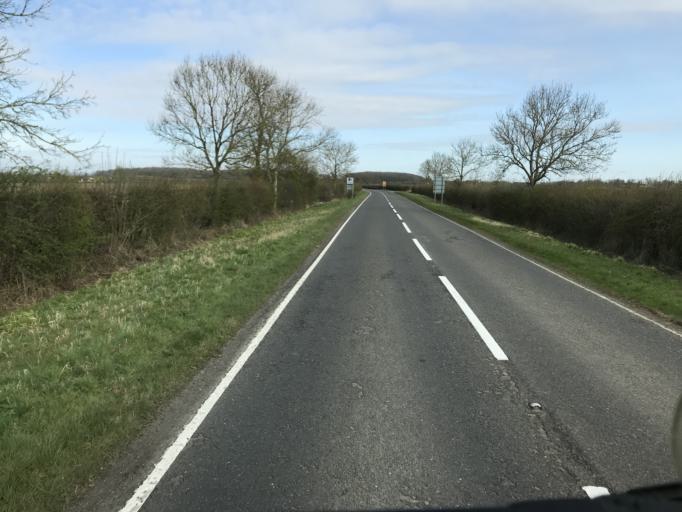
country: GB
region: England
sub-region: Lincolnshire
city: Market Rasen
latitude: 53.3961
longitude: -0.4184
